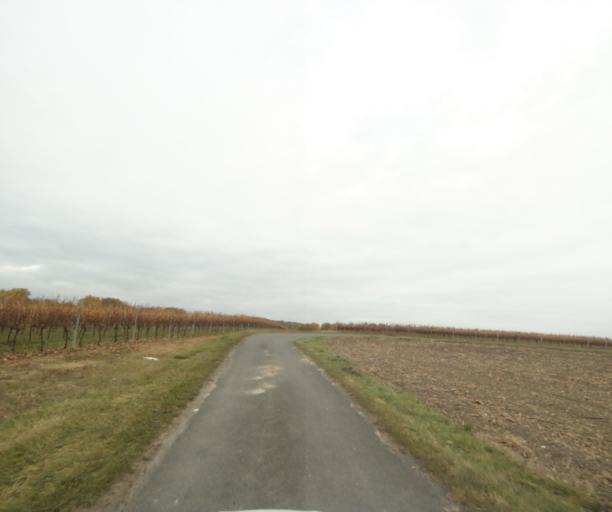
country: FR
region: Poitou-Charentes
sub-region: Departement de la Charente-Maritime
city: Chermignac
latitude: 45.7128
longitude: -0.6789
